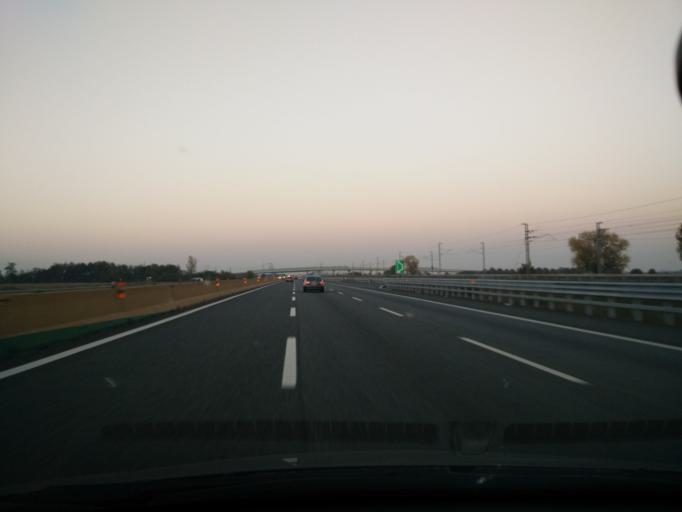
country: IT
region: Piedmont
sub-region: Provincia di Vercelli
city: Saluggia
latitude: 45.2715
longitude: 8.0188
